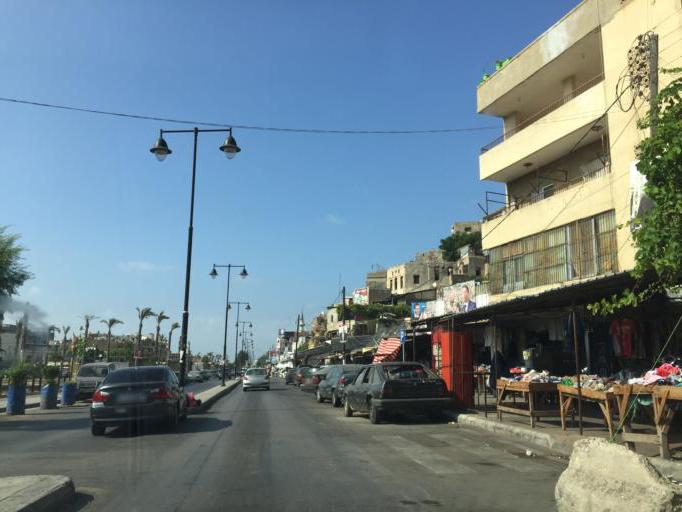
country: LB
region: Liban-Nord
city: Tripoli
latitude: 34.4364
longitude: 35.8469
